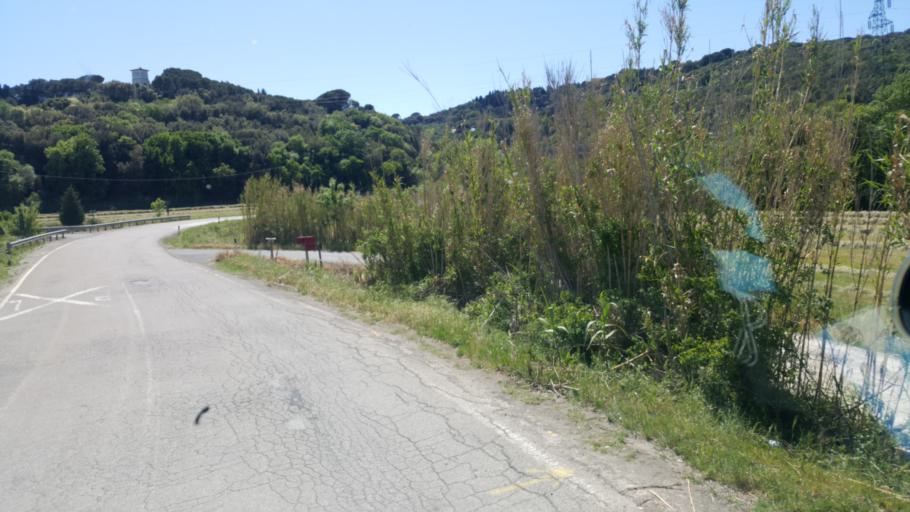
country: IT
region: Tuscany
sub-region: Provincia di Livorno
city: Rosignano Marittimo
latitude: 43.4077
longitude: 10.4956
